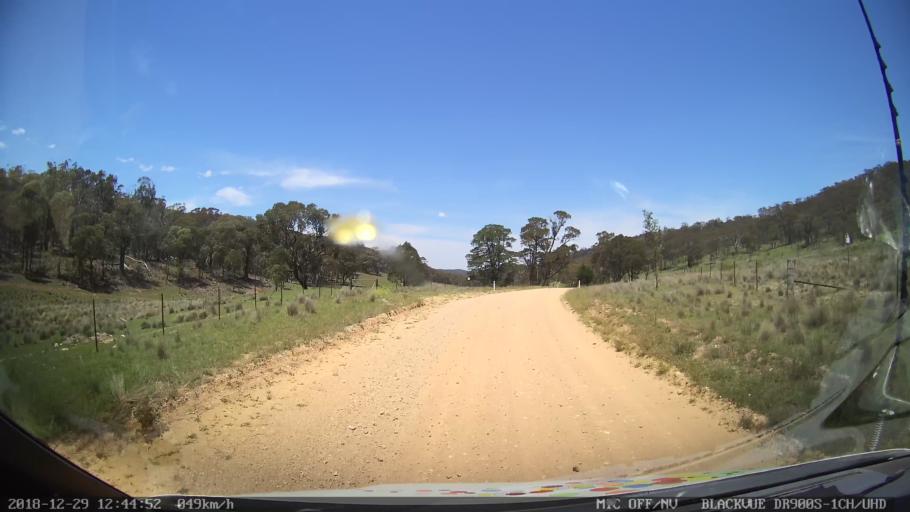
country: AU
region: Australian Capital Territory
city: Macarthur
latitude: -35.6308
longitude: 149.2157
